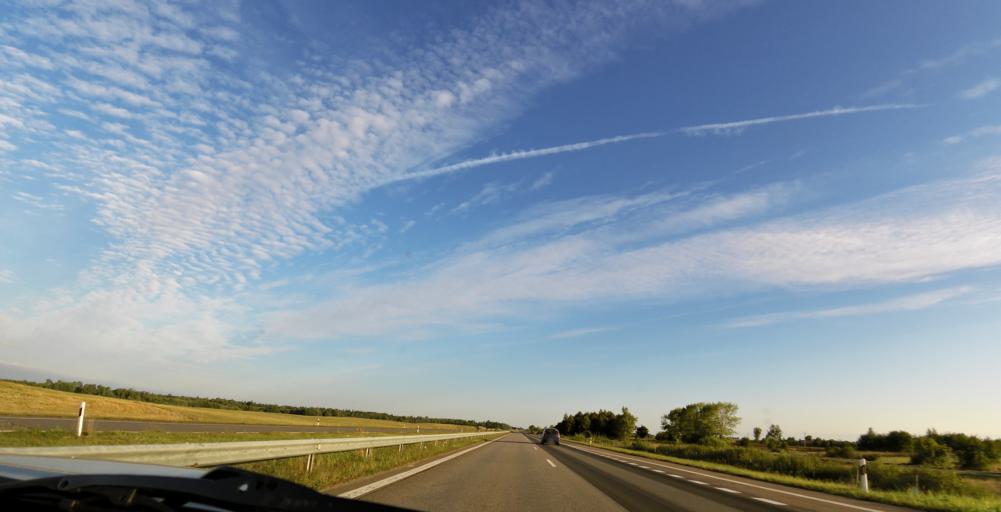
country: LT
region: Vilnius County
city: Ukmerge
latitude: 55.1616
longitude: 24.8189
